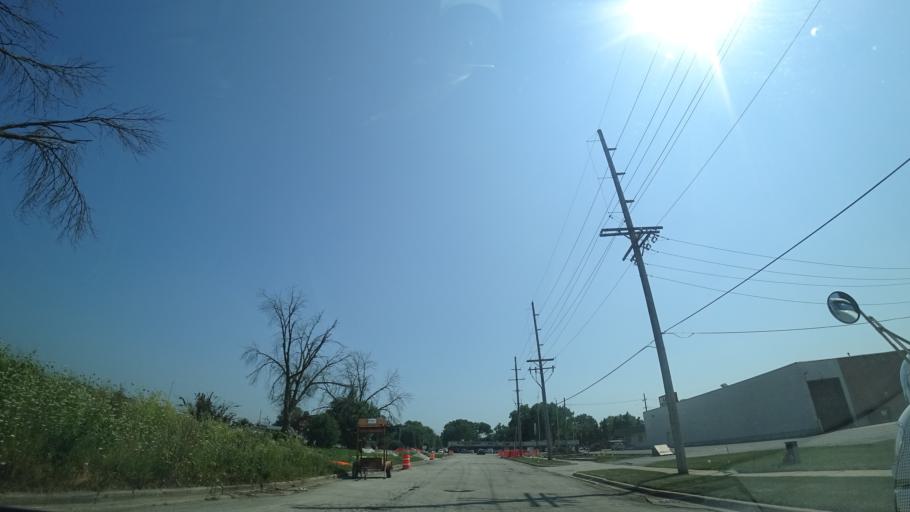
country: US
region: Illinois
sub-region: Cook County
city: Oak Lawn
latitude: 41.6919
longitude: -87.7447
